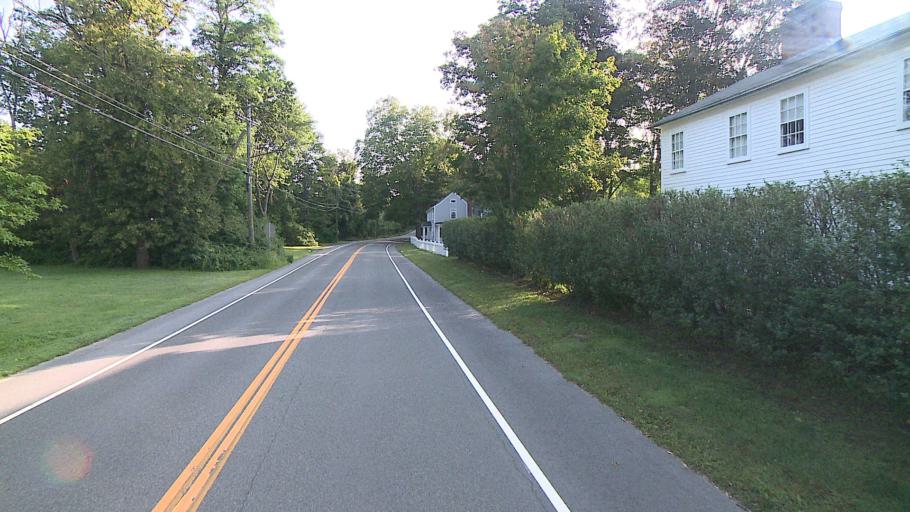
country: US
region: Connecticut
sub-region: Litchfield County
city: Kent
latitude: 41.7306
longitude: -73.4726
